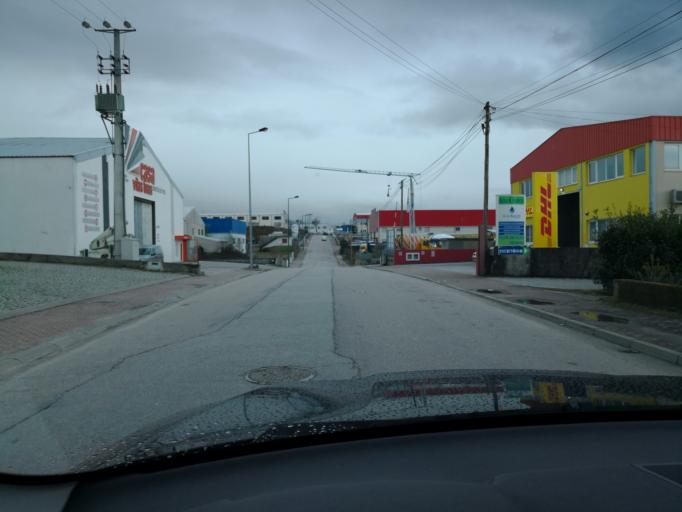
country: PT
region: Vila Real
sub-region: Vila Real
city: Vila Real
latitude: 41.2793
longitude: -7.7090
